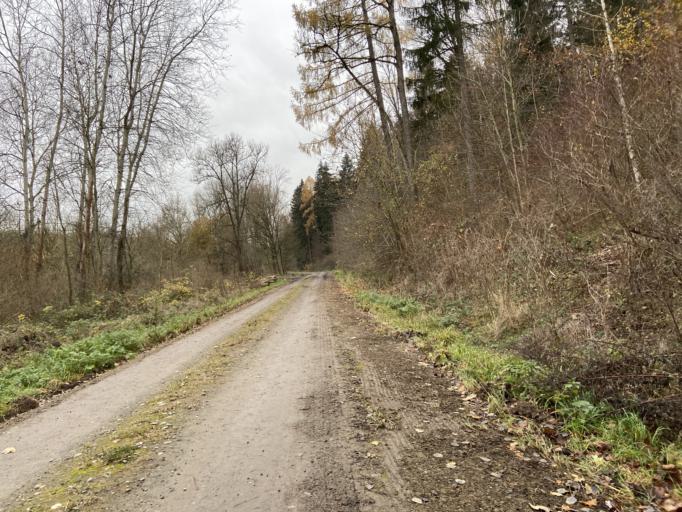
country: DE
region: Lower Saxony
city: Erkerode
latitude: 52.2187
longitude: 10.7175
